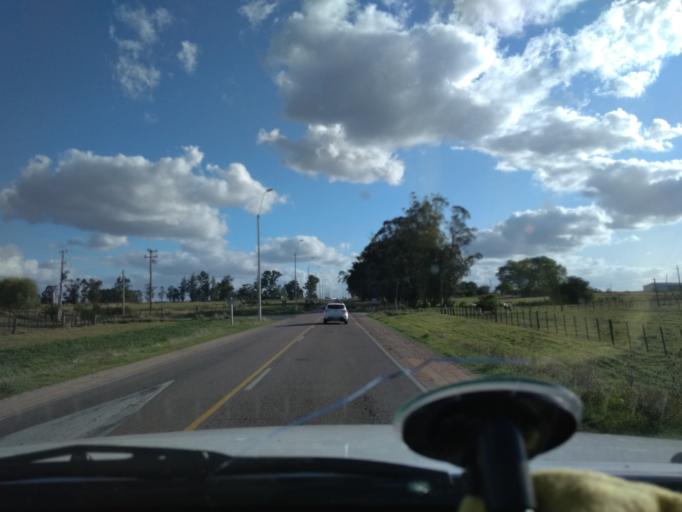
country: UY
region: Canelones
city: Tala
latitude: -34.3563
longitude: -55.7719
